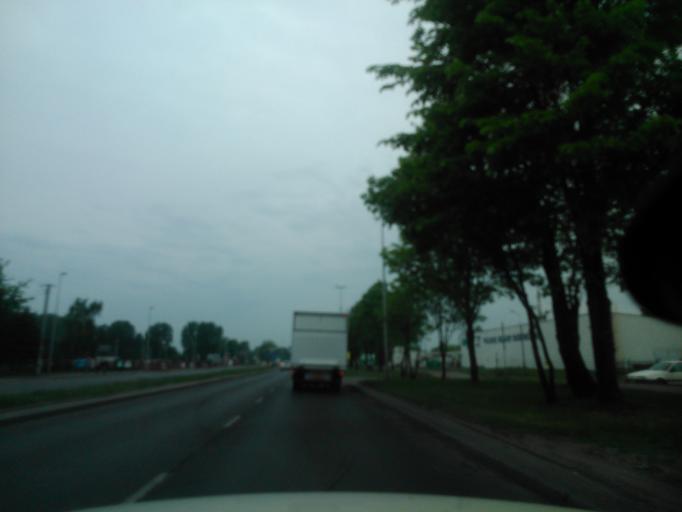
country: PL
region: Kujawsko-Pomorskie
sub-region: Powiat torunski
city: Lubicz Dolny
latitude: 53.0371
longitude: 18.6781
